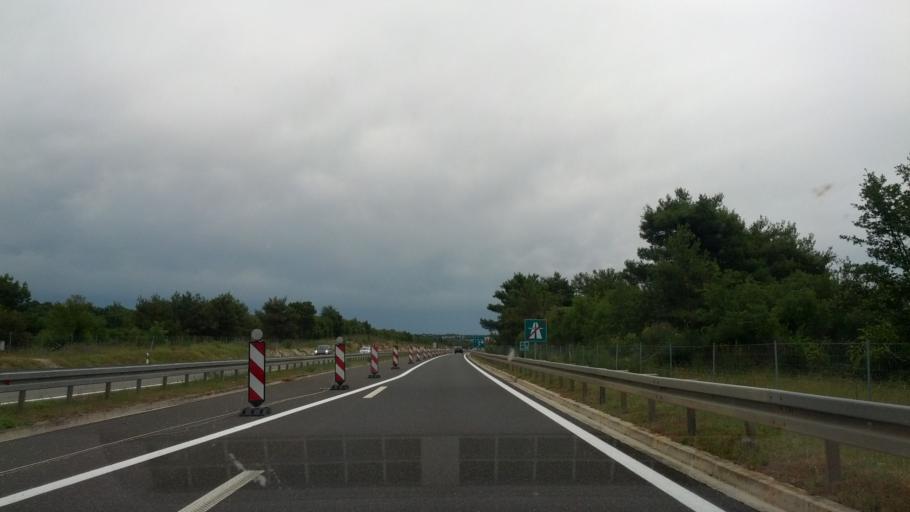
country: HR
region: Istarska
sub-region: Grad Rovinj
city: Rovinj
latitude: 45.1241
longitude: 13.7875
